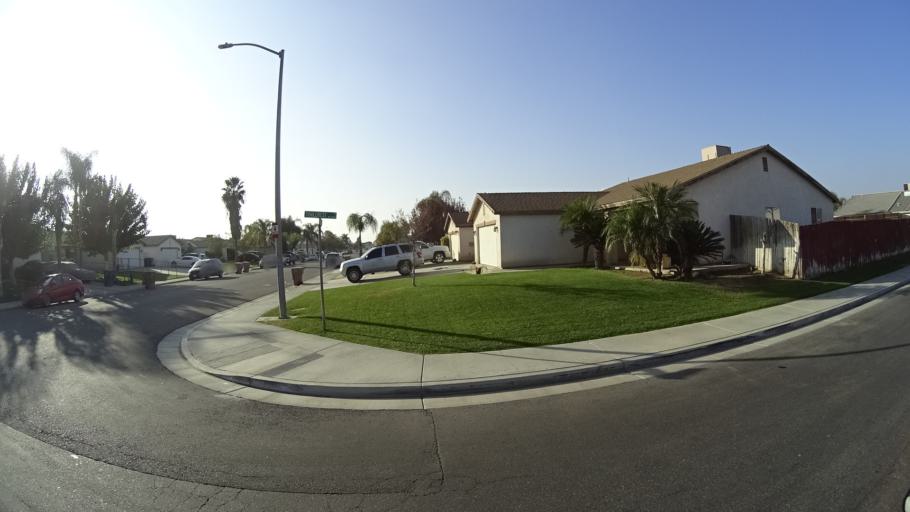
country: US
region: California
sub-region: Kern County
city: Greenfield
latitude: 35.2863
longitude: -119.0163
